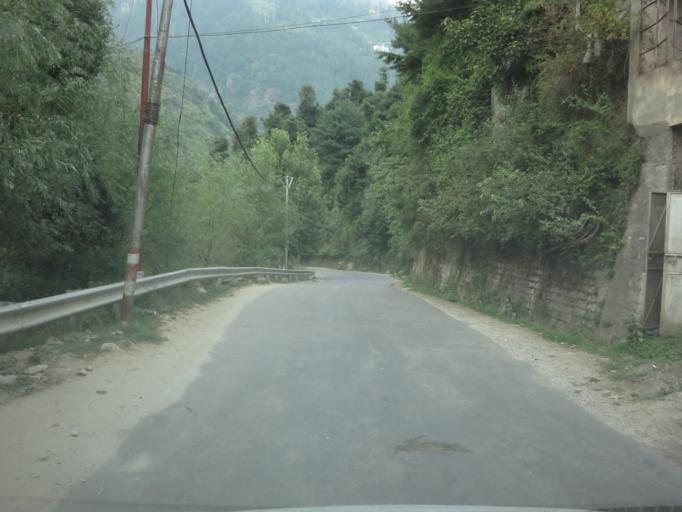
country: IN
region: Himachal Pradesh
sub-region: Kulu
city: Manali
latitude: 32.2252
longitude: 77.1959
